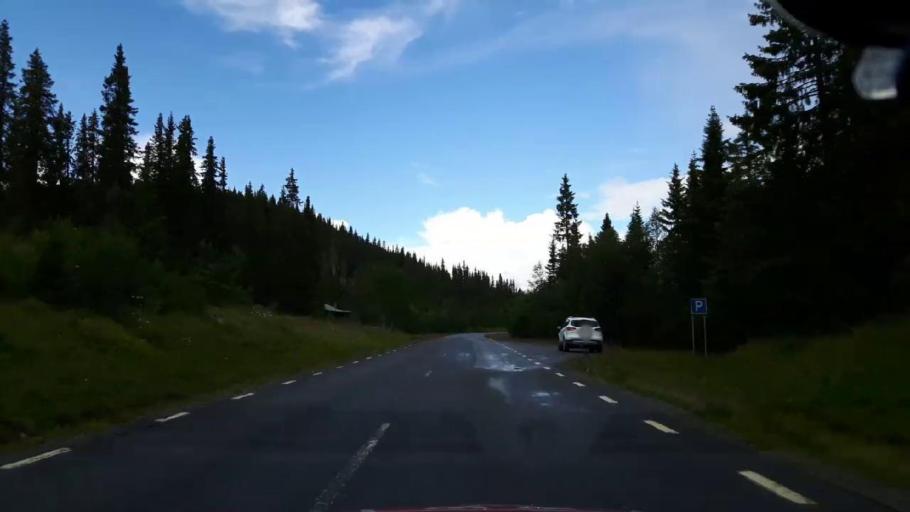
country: SE
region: Vaesterbotten
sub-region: Vilhelmina Kommun
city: Sjoberg
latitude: 64.9975
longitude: 15.2035
